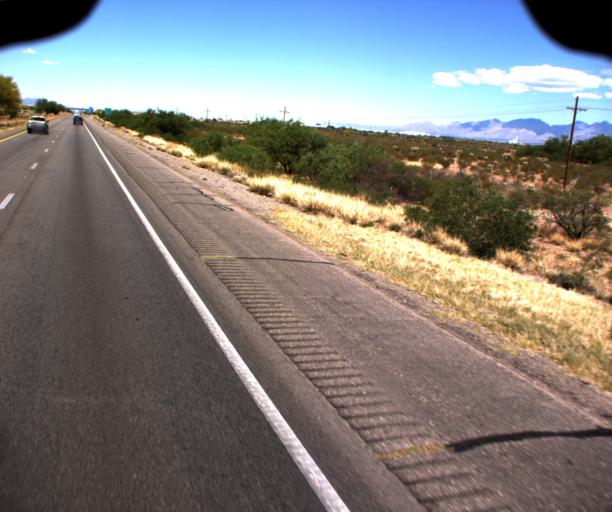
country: US
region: Arizona
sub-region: Pima County
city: Vail
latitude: 32.0778
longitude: -110.7993
